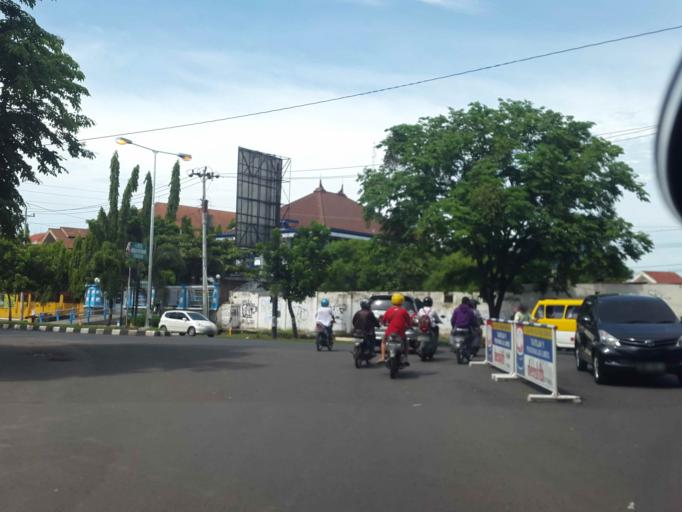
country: ID
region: Central Java
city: Semarang
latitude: -6.9871
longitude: 110.3853
